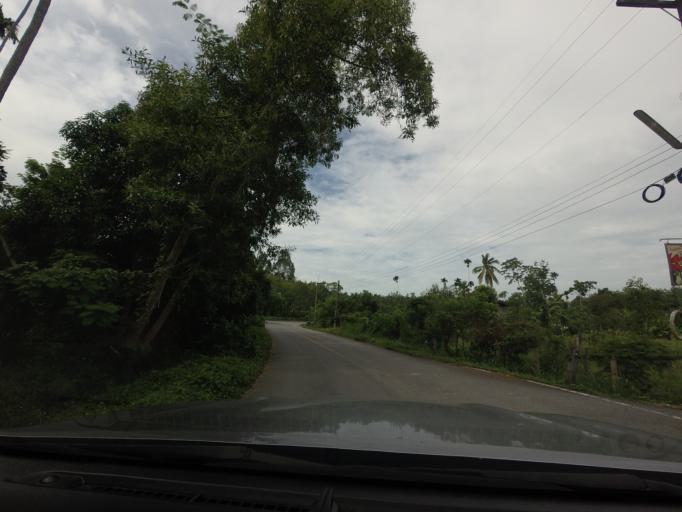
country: TH
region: Nakhon Si Thammarat
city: Phra Phrom
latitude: 8.2837
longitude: 99.9141
